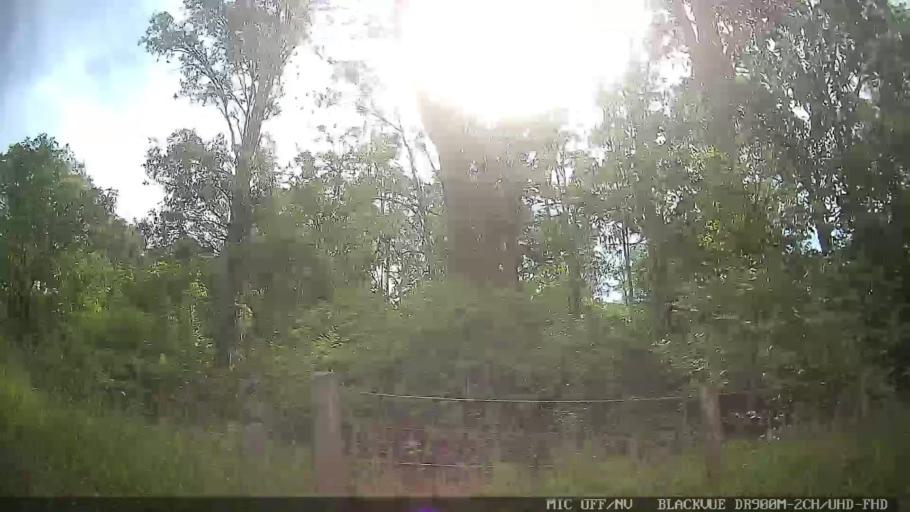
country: BR
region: Sao Paulo
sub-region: Conchas
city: Conchas
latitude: -23.0435
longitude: -47.9940
